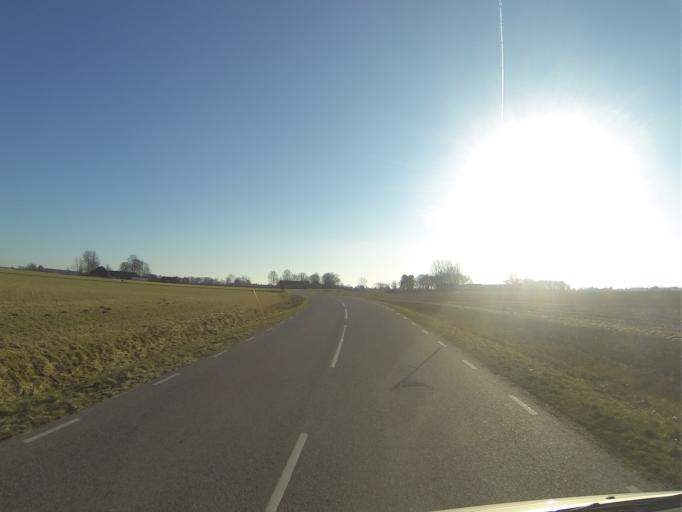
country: SE
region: Skane
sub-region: Hoors Kommun
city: Loberod
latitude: 55.7875
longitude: 13.5323
